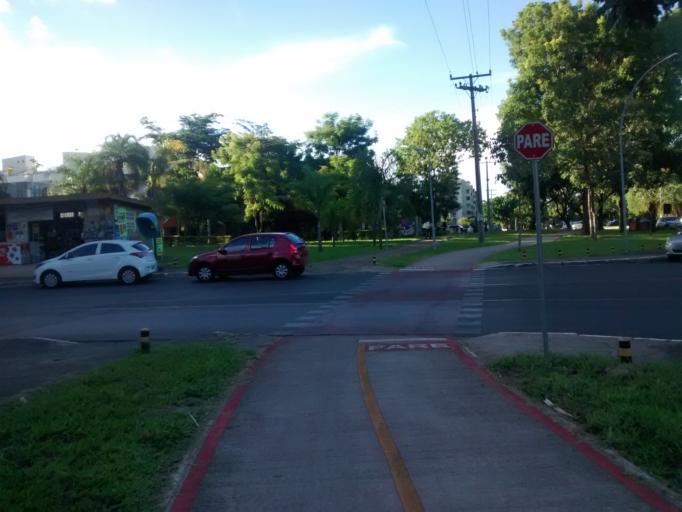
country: BR
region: Federal District
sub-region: Brasilia
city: Brasilia
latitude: -15.7582
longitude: -47.8820
